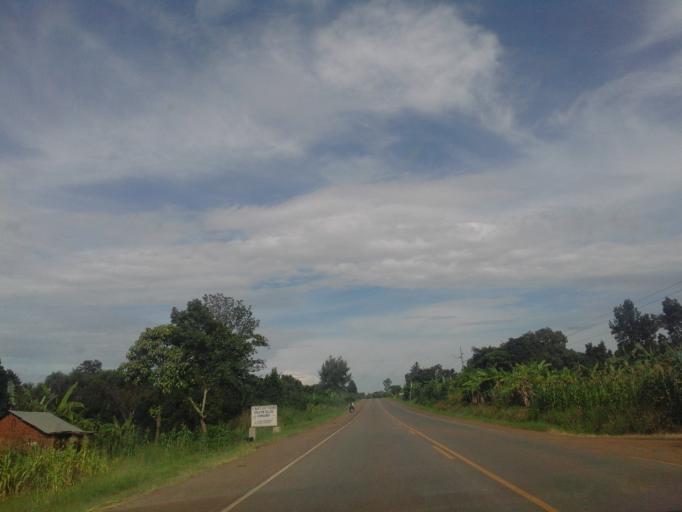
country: UG
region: Central Region
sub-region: Lwengo District
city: Lwengo
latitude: -0.3680
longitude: 31.5348
